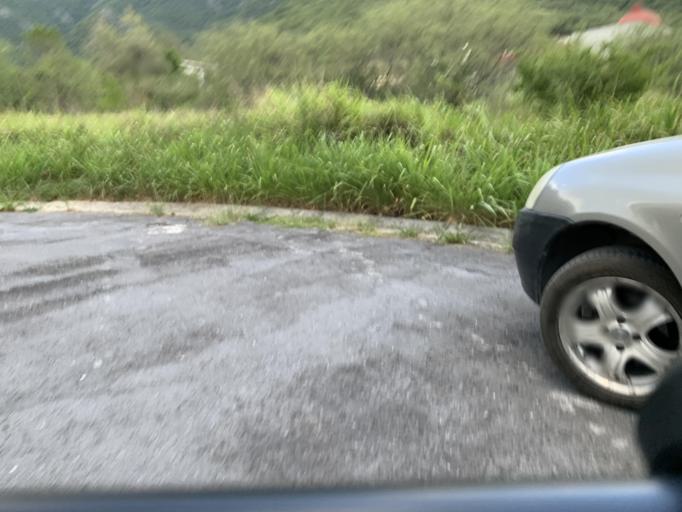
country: MX
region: Nuevo Leon
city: Santiago
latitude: 25.5063
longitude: -100.1799
